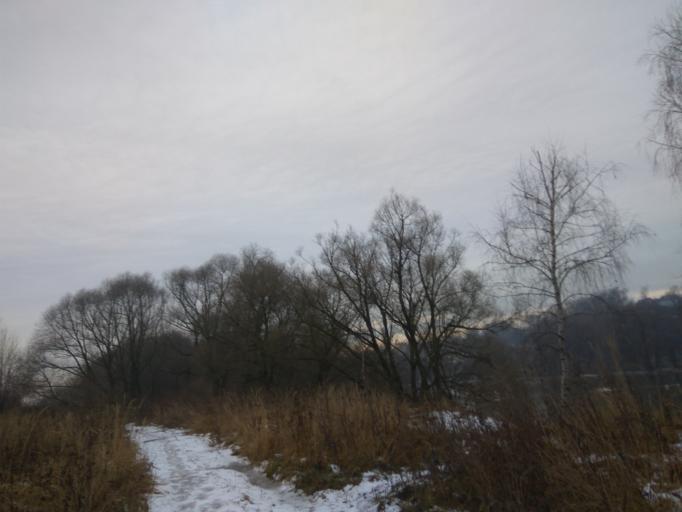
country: RU
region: Moskovskaya
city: Gorki-Leninskiye
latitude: 55.4798
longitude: 37.7934
